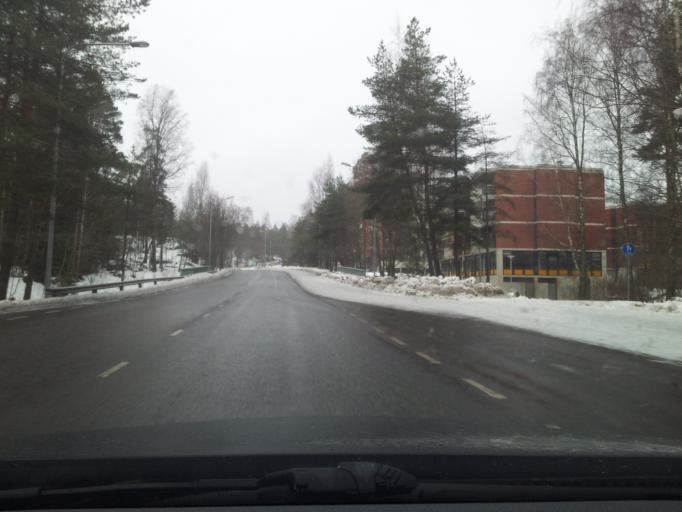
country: FI
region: Uusimaa
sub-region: Helsinki
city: Kauniainen
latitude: 60.1729
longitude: 24.7223
